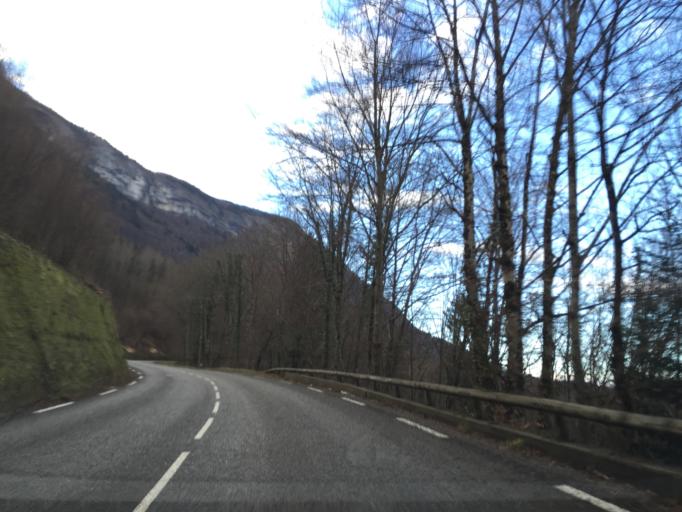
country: FR
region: Rhone-Alpes
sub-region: Departement de la Haute-Savoie
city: Gruffy
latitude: 45.7470
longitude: 6.0796
